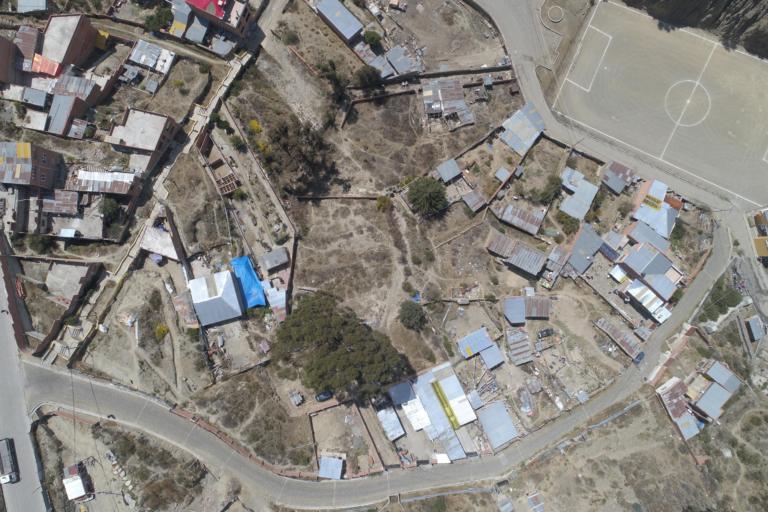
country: BO
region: La Paz
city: La Paz
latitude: -16.4994
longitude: -68.0994
